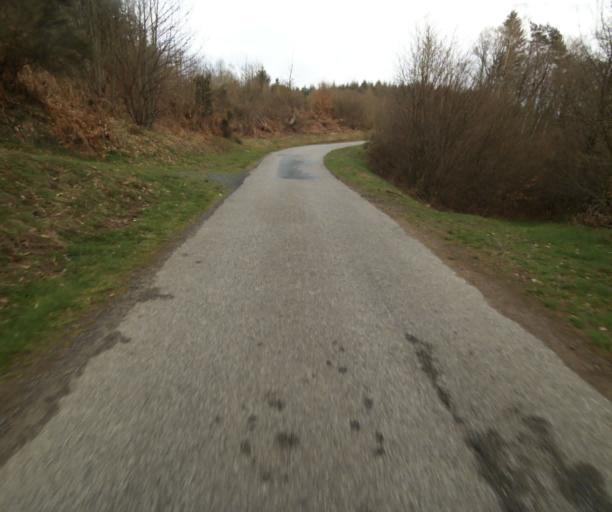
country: FR
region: Limousin
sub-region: Departement de la Correze
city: Saint-Privat
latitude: 45.2264
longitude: 1.9946
